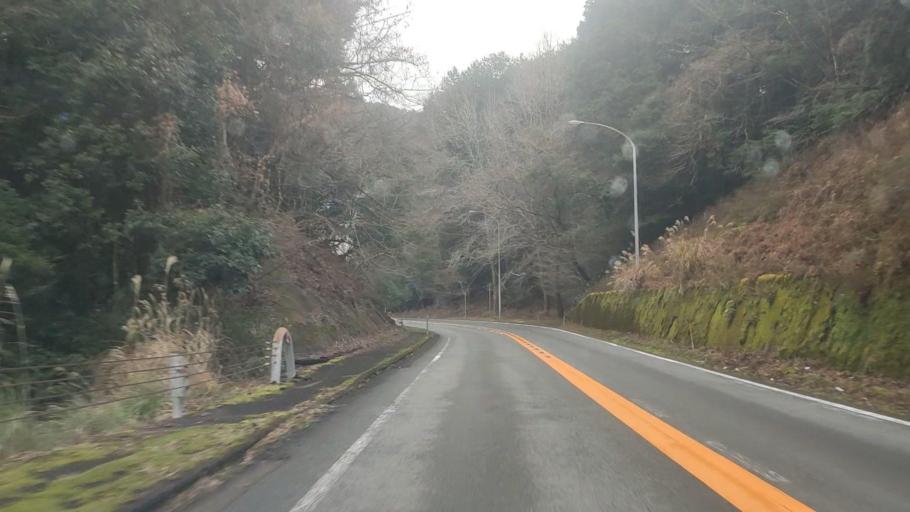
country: JP
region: Kumamoto
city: Hitoyoshi
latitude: 32.1214
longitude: 130.8102
